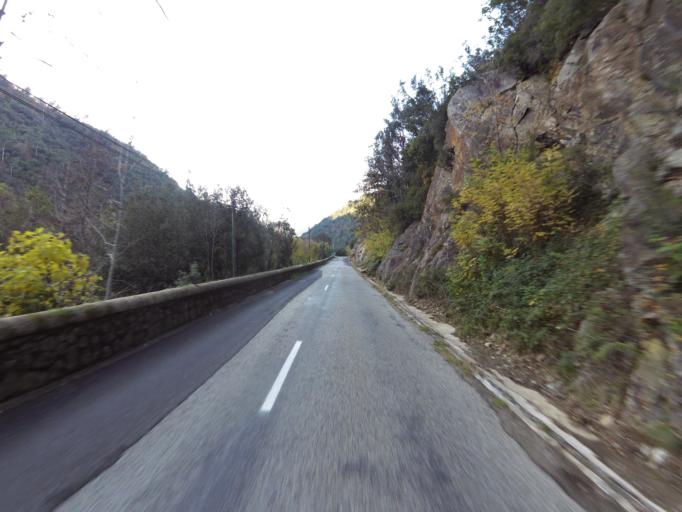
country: FR
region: Rhone-Alpes
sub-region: Departement de l'Ardeche
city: Lablachere
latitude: 44.5124
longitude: 4.2009
